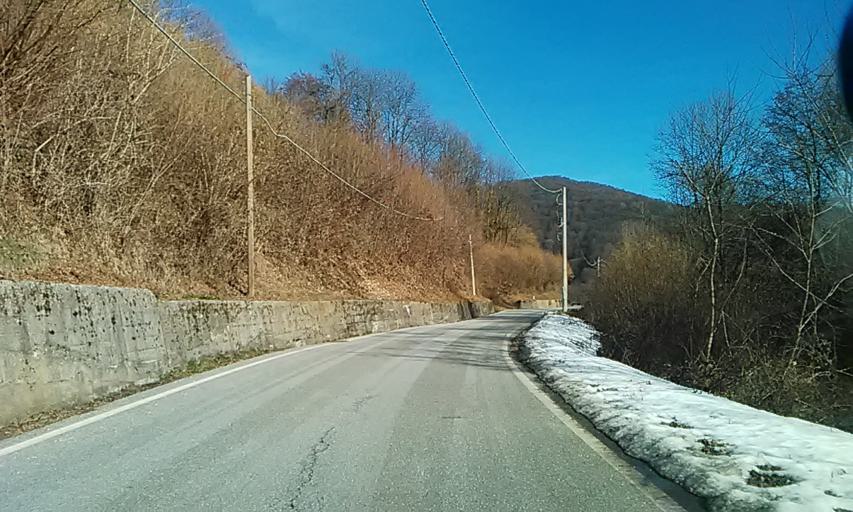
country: IT
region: Piedmont
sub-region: Provincia di Vercelli
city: Cellio
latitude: 45.7596
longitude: 8.3138
